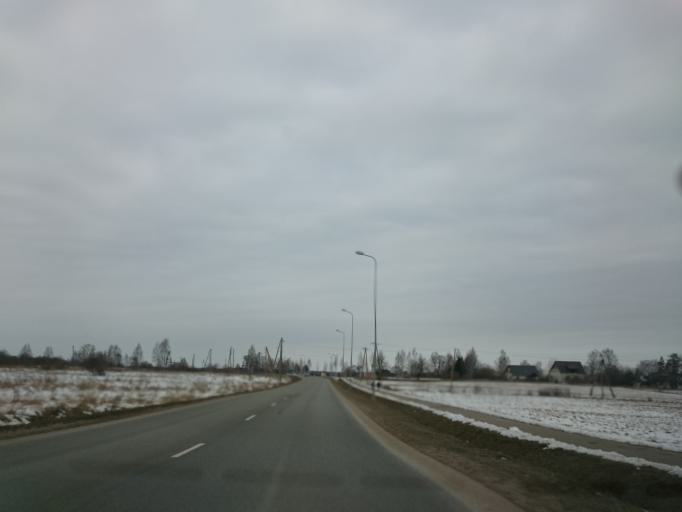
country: LV
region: Cesu Rajons
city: Cesis
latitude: 57.2992
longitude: 25.2461
